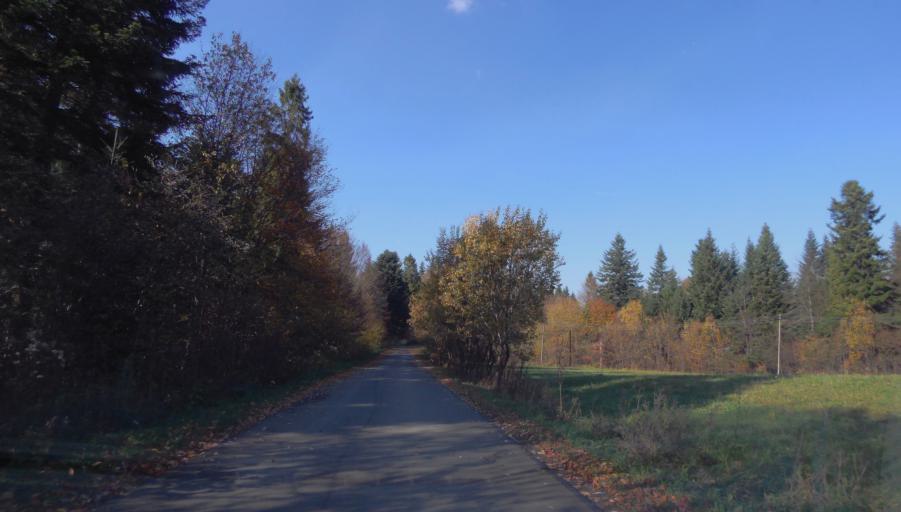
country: PL
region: Subcarpathian Voivodeship
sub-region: Powiat leski
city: Polanczyk
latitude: 49.3149
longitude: 22.4444
